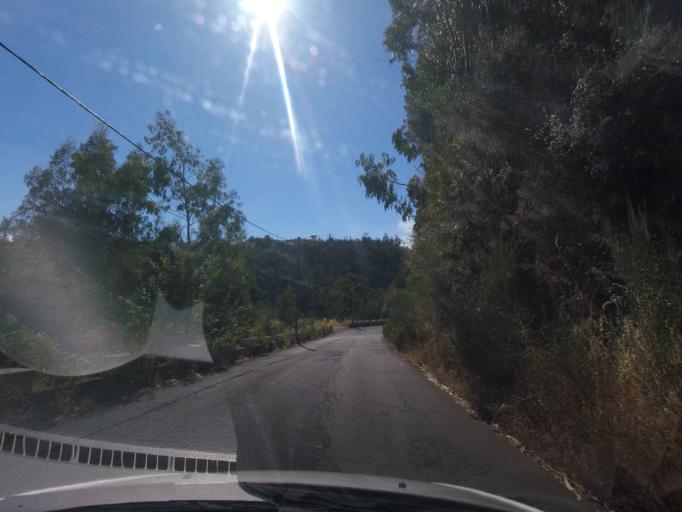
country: PT
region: Madeira
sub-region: Santa Cruz
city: Camacha
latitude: 32.6895
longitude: -16.8469
